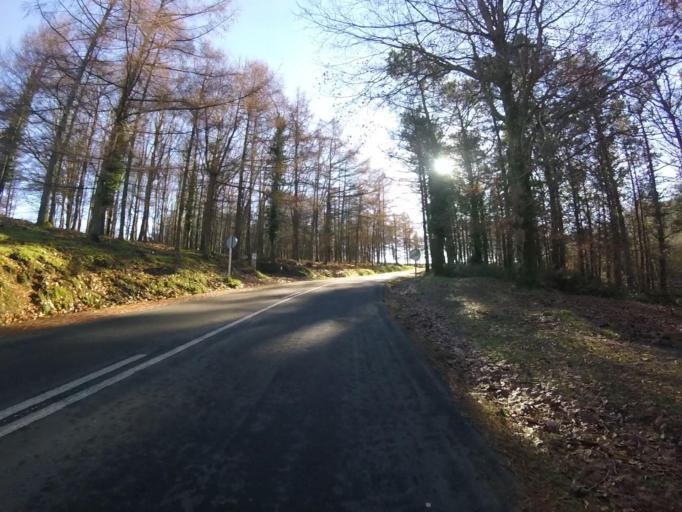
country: ES
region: Basque Country
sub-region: Provincia de Guipuzcoa
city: Irun
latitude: 43.3082
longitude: -1.7555
